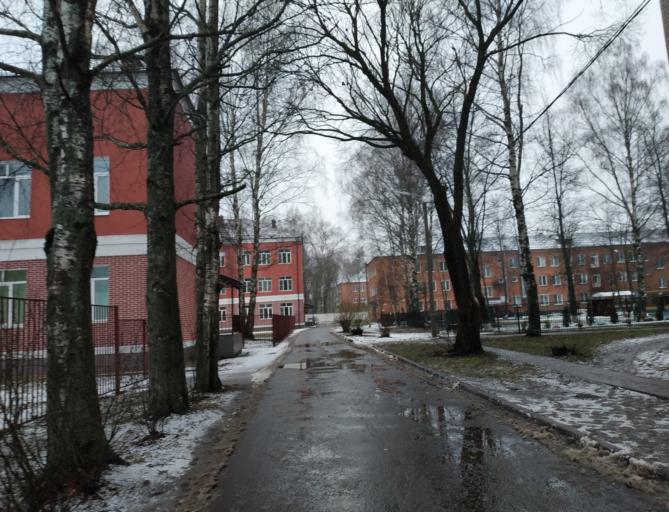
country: RU
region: Moskovskaya
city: Taldom
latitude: 56.7416
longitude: 37.5361
